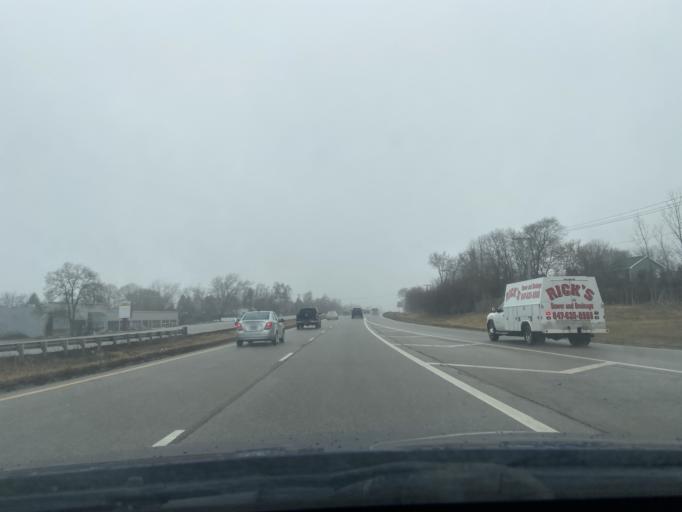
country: US
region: Illinois
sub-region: Lake County
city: Wauconda
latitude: 42.2610
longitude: -88.1542
